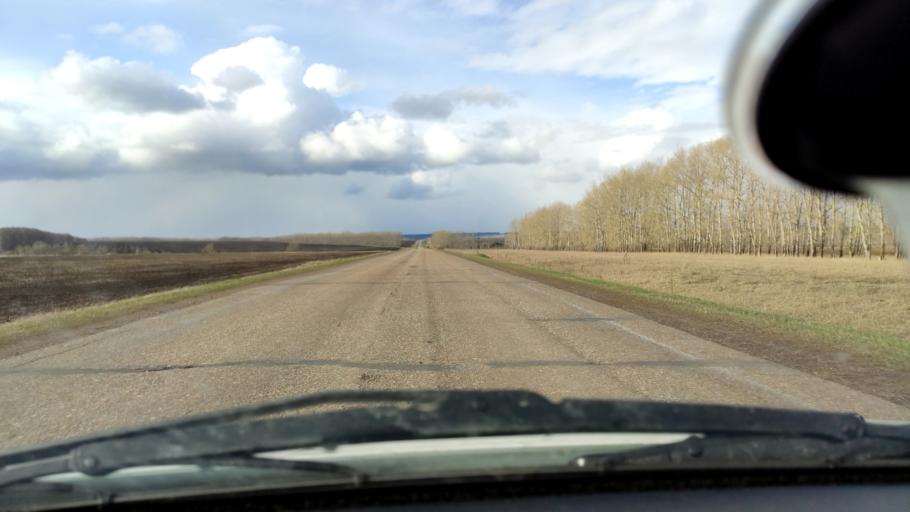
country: RU
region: Bashkortostan
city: Buzdyak
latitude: 54.7394
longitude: 54.5659
